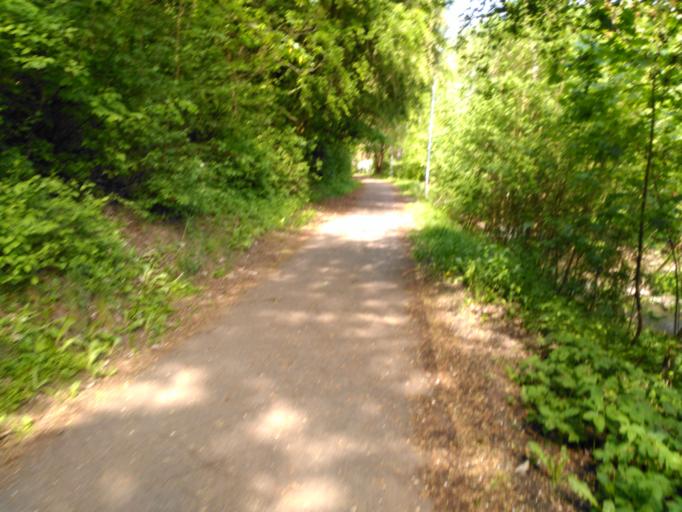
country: CZ
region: Central Bohemia
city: Cernosice
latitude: 49.9887
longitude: 14.3504
